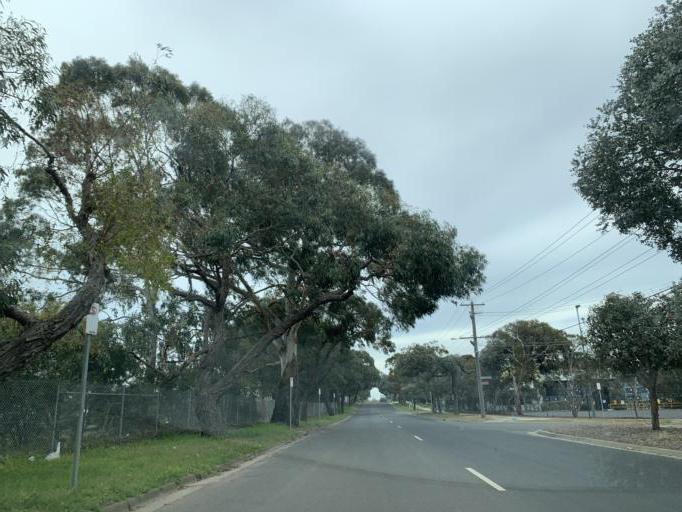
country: AU
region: Victoria
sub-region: Bayside
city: Highett
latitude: -37.9610
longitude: 145.0327
